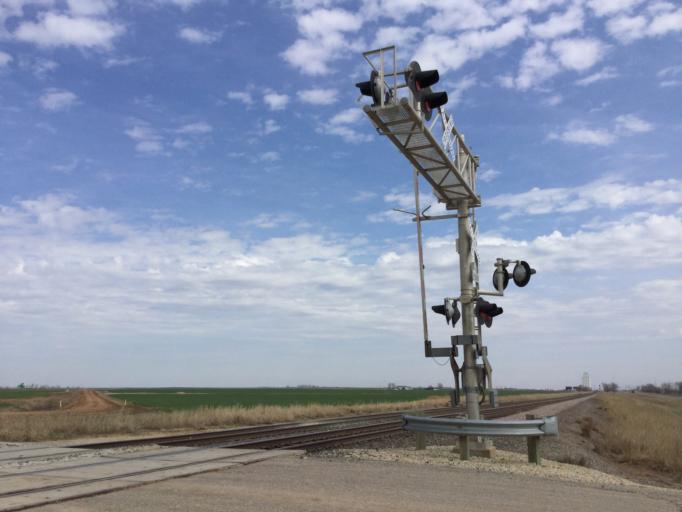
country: US
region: Kansas
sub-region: Barber County
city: Kiowa
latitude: 37.0810
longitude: -98.4211
